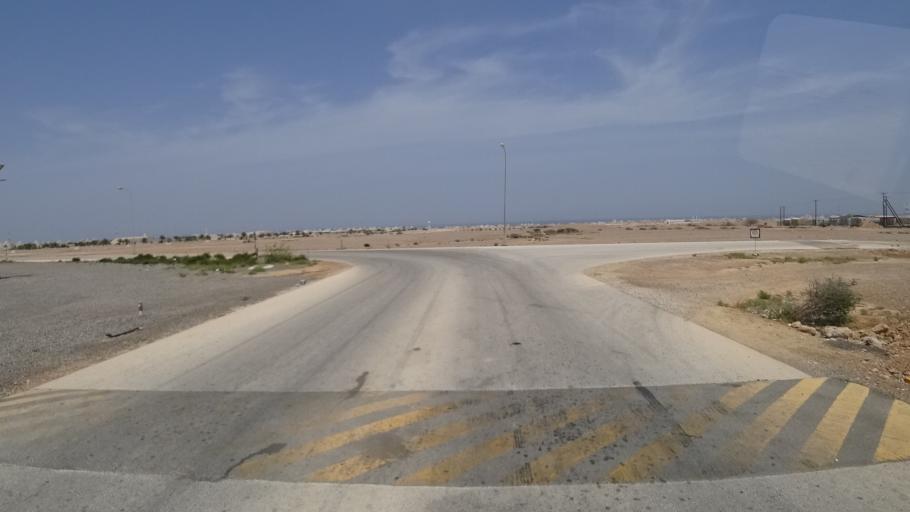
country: OM
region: Ash Sharqiyah
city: Sur
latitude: 22.5997
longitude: 59.4387
